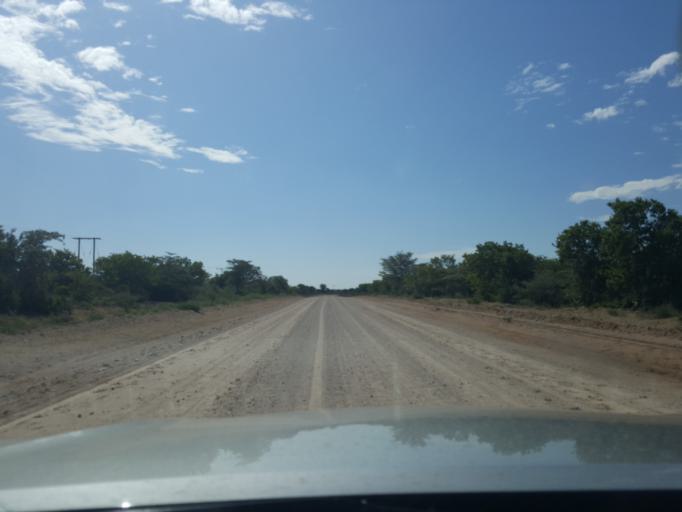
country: BW
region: Kweneng
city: Khudumelapye
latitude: -23.7807
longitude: 24.7741
